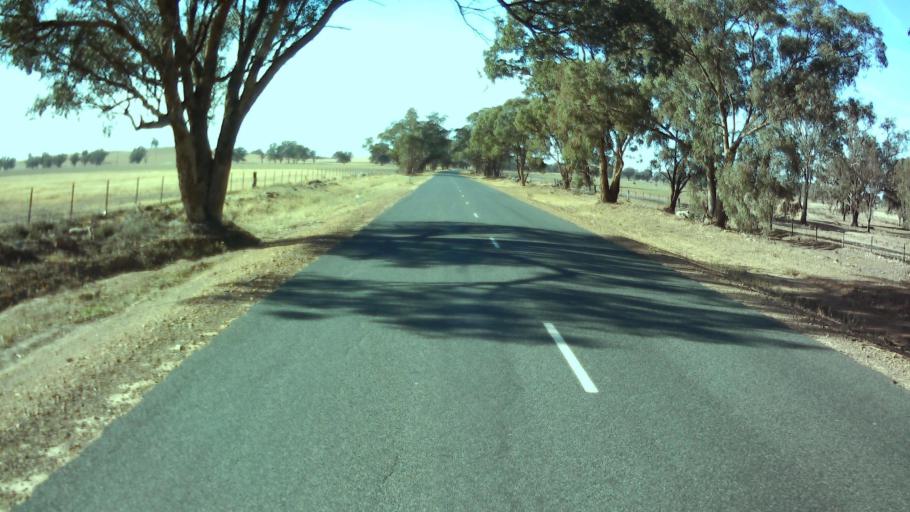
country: AU
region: New South Wales
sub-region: Weddin
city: Grenfell
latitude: -33.9545
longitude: 148.1390
